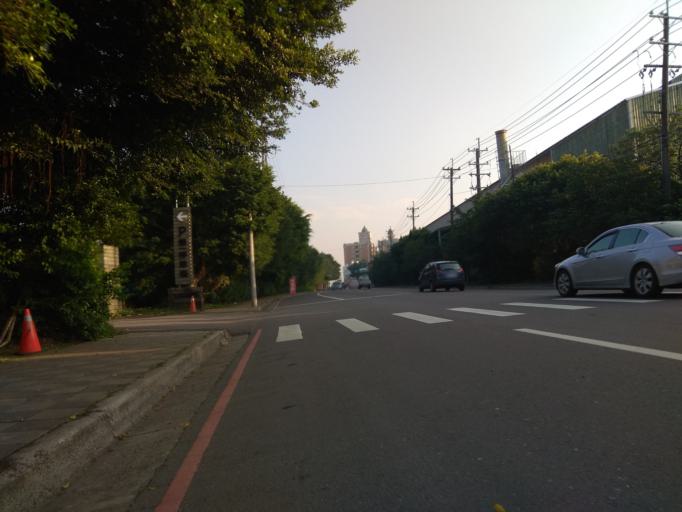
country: TW
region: Taiwan
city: Daxi
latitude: 24.9255
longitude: 121.1759
